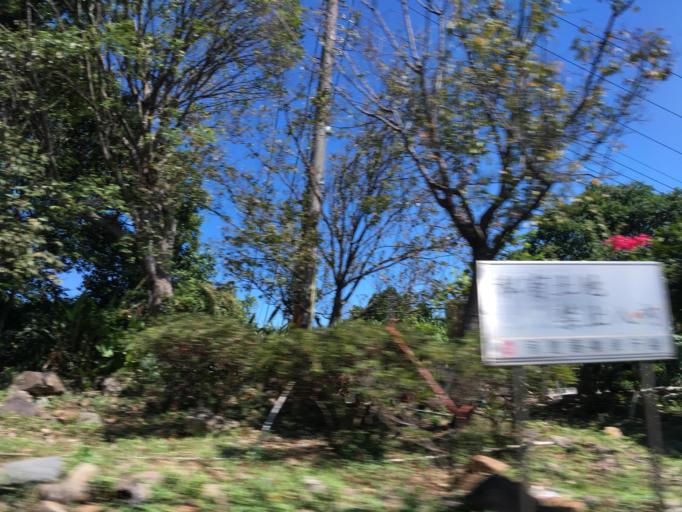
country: TW
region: Taipei
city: Taipei
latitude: 25.1493
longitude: 121.5044
